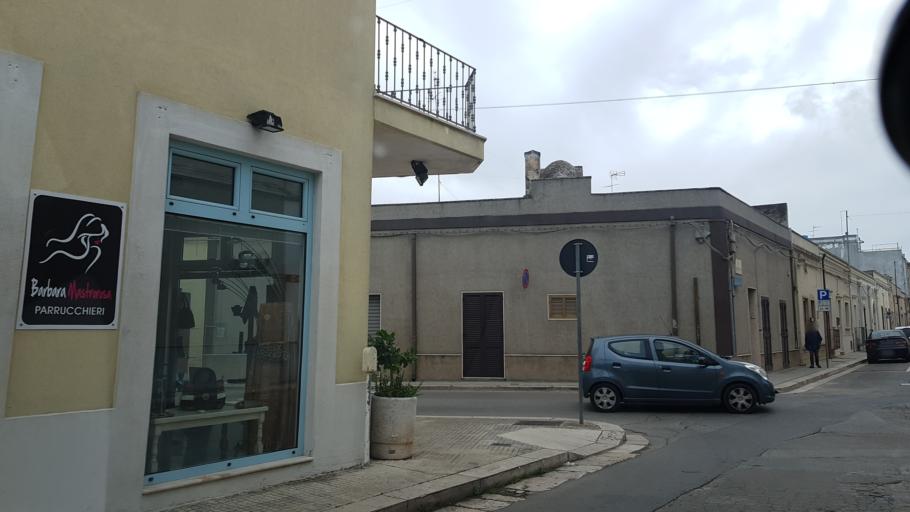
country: IT
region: Apulia
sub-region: Provincia di Brindisi
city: Mesagne
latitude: 40.5627
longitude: 17.8109
